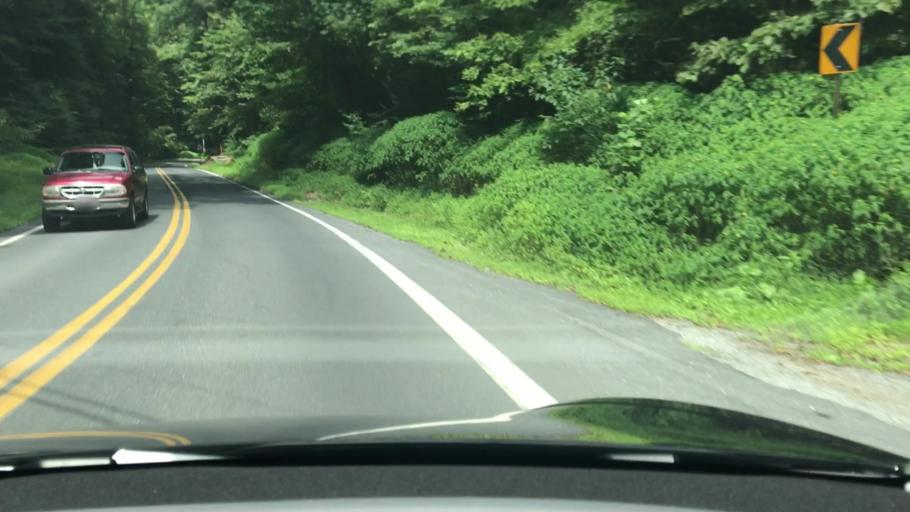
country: US
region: Pennsylvania
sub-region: Cumberland County
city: New Cumberland
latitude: 40.1898
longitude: -76.8725
